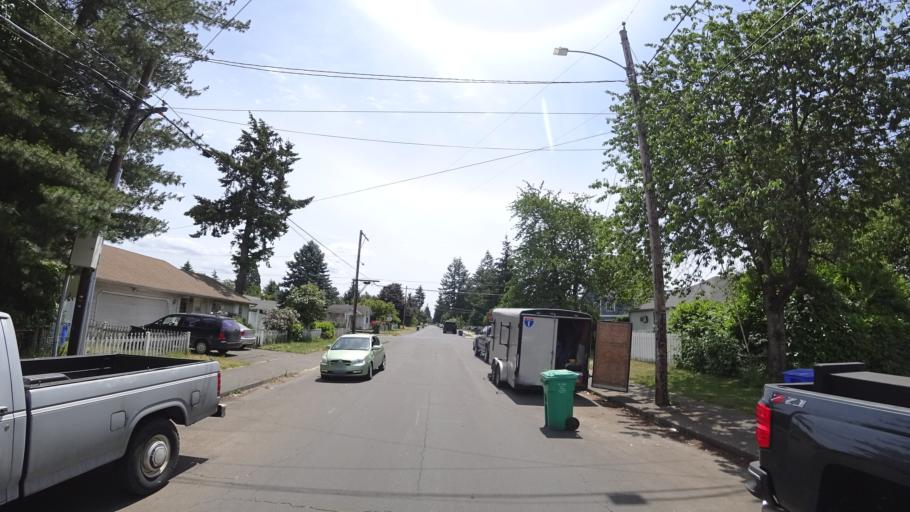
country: US
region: Oregon
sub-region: Multnomah County
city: Lents
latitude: 45.4763
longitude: -122.5997
